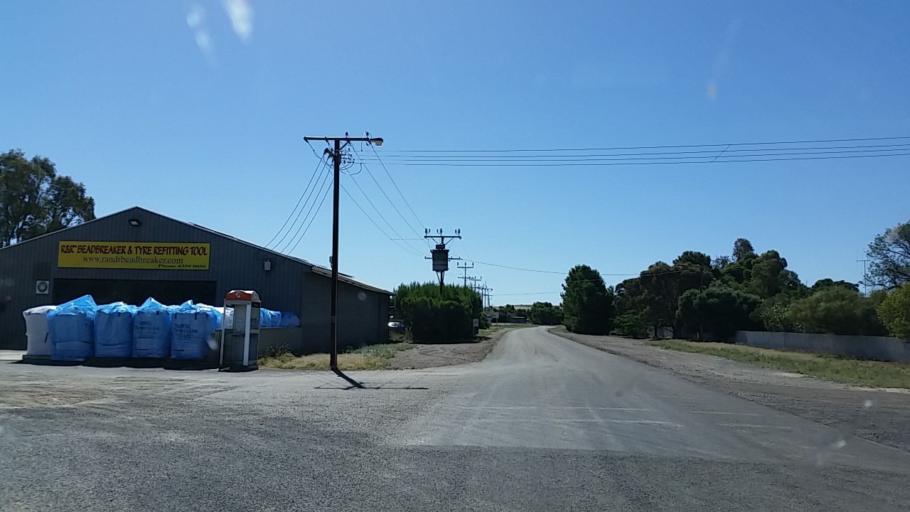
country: AU
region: South Australia
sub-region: Peterborough
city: Peterborough
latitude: -33.1533
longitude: 138.9226
